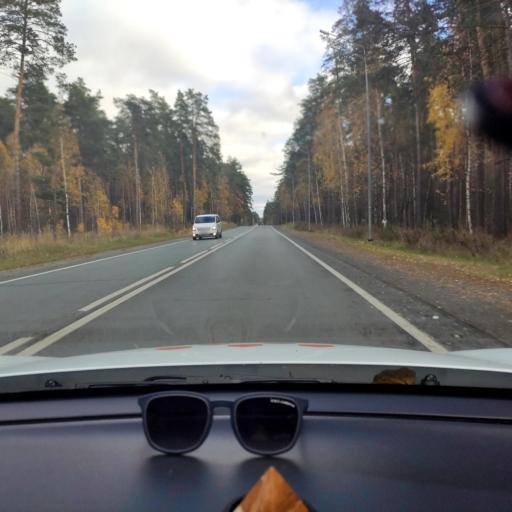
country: RU
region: Tatarstan
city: Stolbishchi
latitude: 55.6355
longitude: 49.0733
